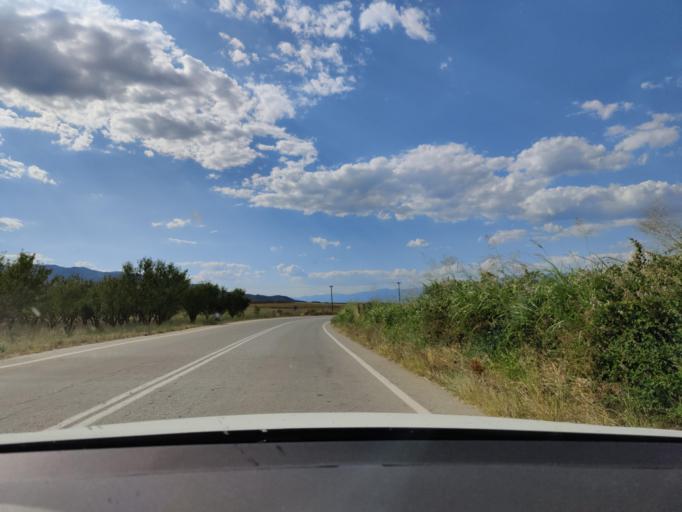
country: GR
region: Central Macedonia
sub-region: Nomos Serron
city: Strymoniko
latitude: 41.0955
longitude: 23.2713
